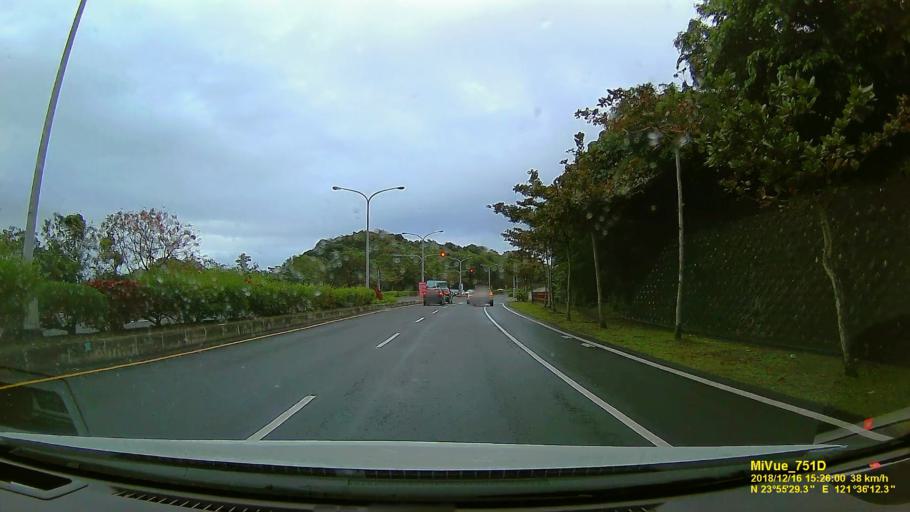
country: TW
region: Taiwan
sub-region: Hualien
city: Hualian
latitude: 23.9251
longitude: 121.6036
